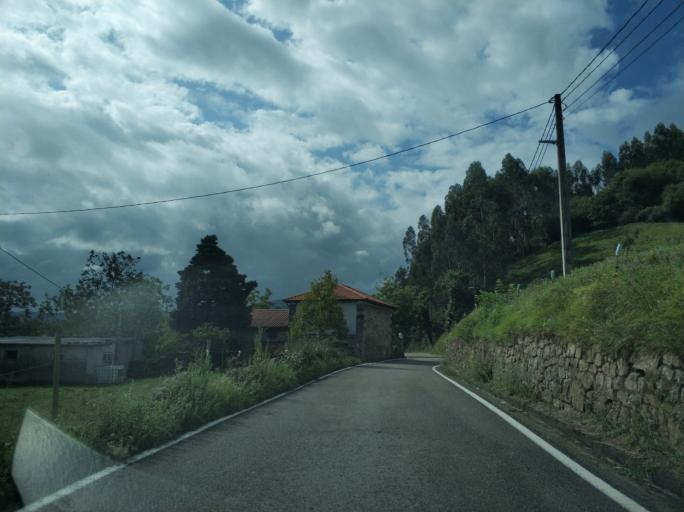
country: ES
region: Cantabria
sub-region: Provincia de Cantabria
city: Polanco
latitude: 43.3673
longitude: -3.9684
